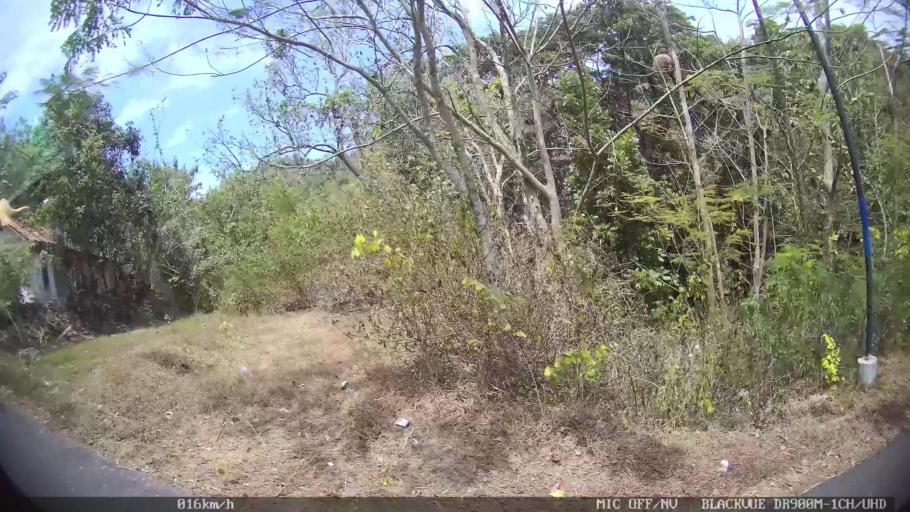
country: ID
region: Central Java
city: Candi Prambanan
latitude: -7.8140
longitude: 110.5132
